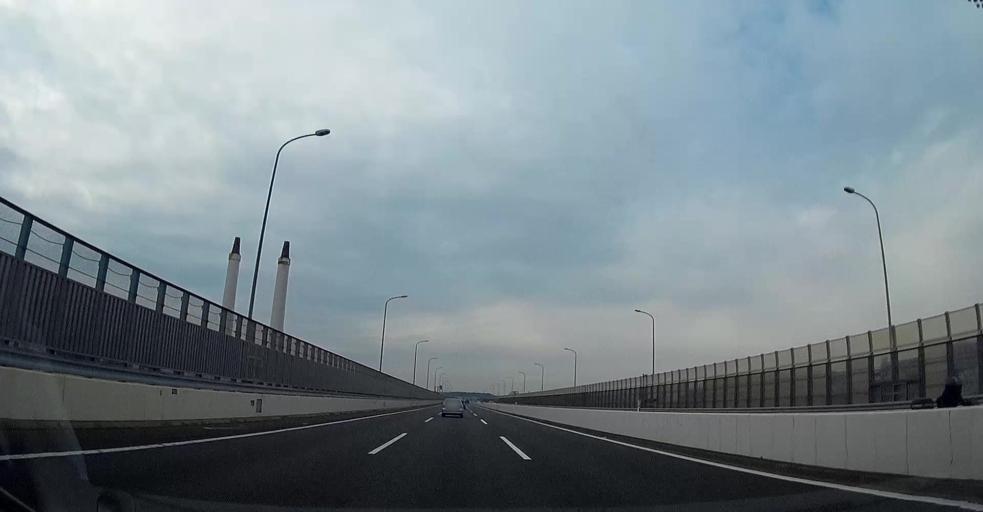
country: JP
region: Kanagawa
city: Yokohama
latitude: 35.4183
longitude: 139.6443
